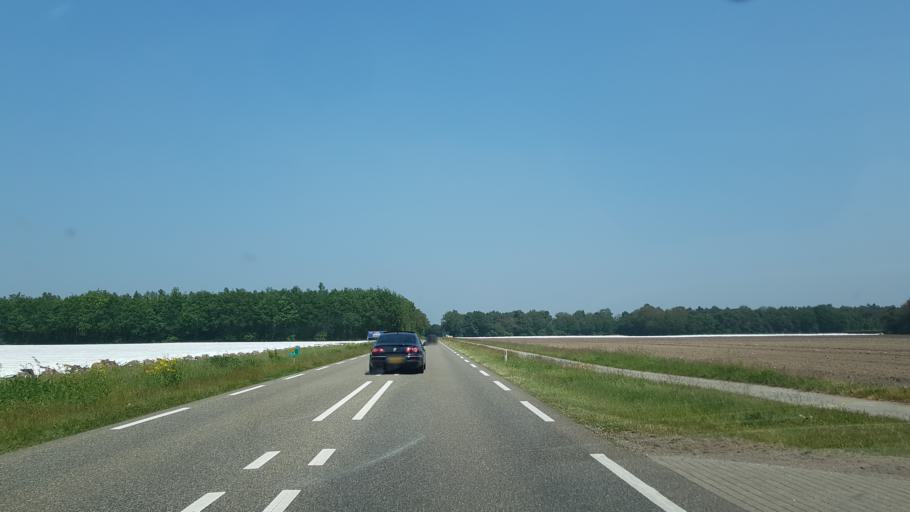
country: NL
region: Limburg
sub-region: Gemeente Peel en Maas
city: Maasbree
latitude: 51.3655
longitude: 5.9780
